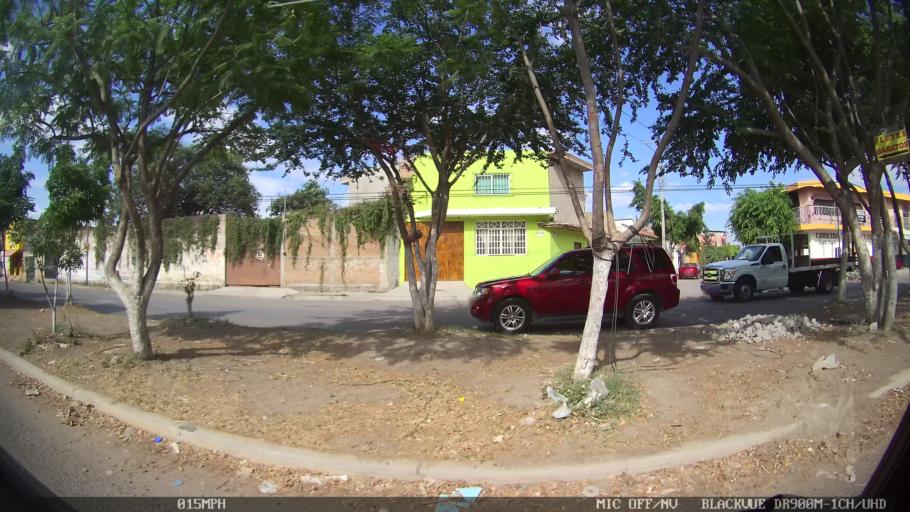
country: MX
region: Jalisco
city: Tonala
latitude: 20.6648
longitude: -103.2522
